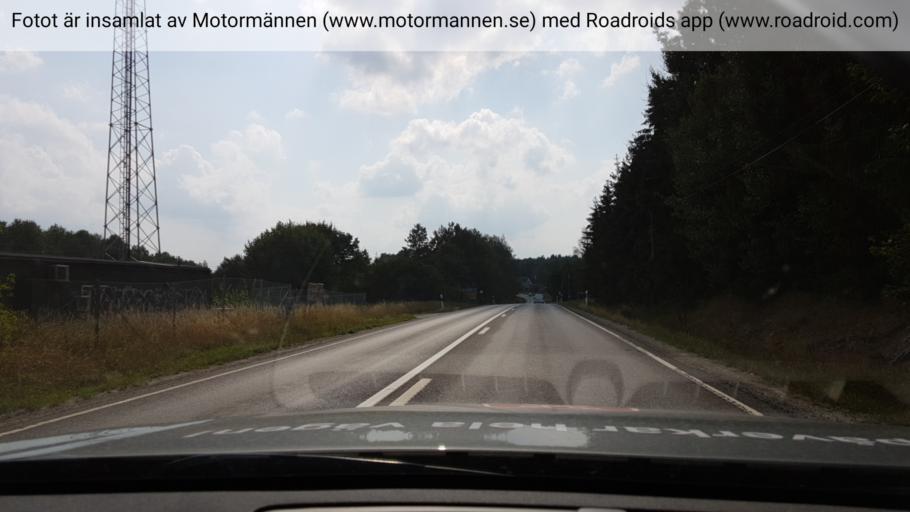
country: SE
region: Stockholm
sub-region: Sodertalje Kommun
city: Molnbo
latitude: 59.0781
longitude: 17.5437
